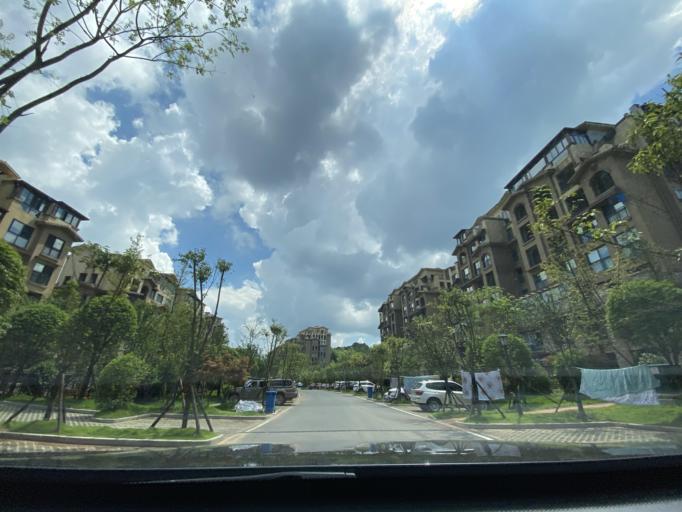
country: CN
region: Guizhou Sheng
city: Changqi
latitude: 28.5370
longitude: 105.9706
